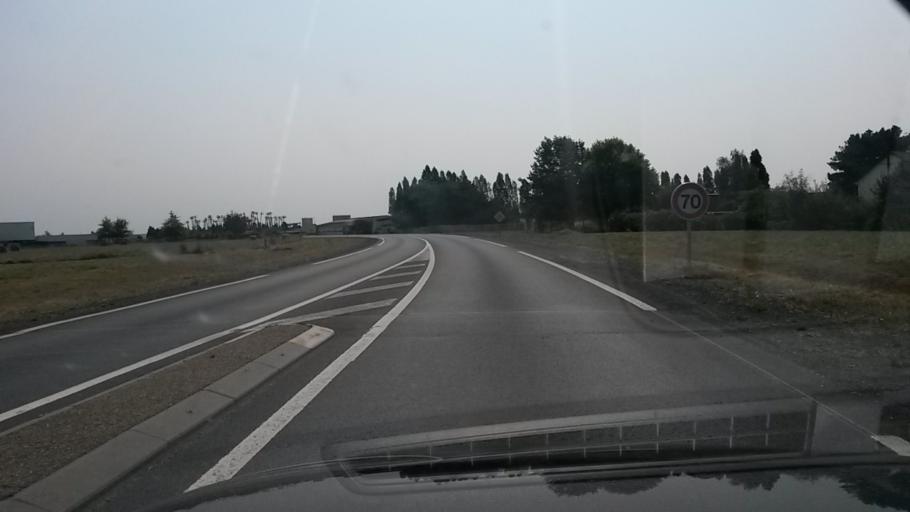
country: FR
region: Pays de la Loire
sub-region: Departement de la Loire-Atlantique
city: Mesanger
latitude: 47.4148
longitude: -1.1890
